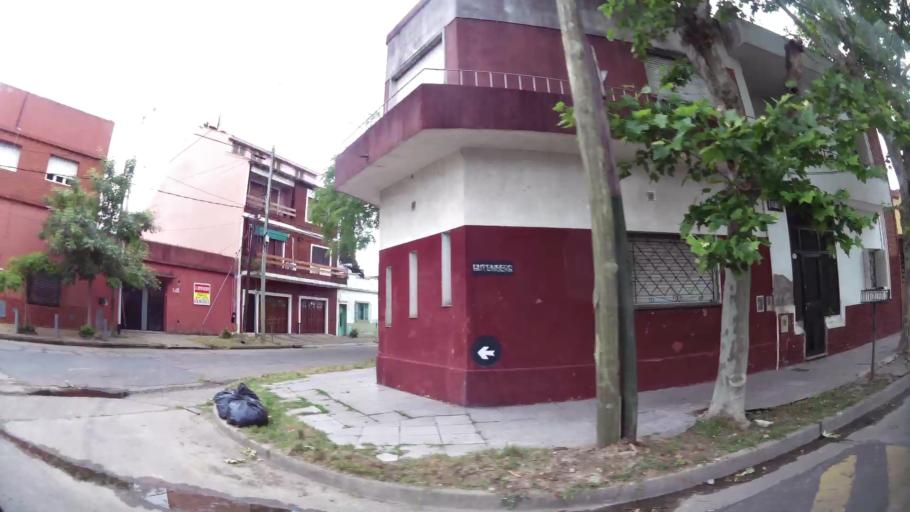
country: AR
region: Buenos Aires
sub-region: Partido de Avellaneda
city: Avellaneda
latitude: -34.6790
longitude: -58.3819
